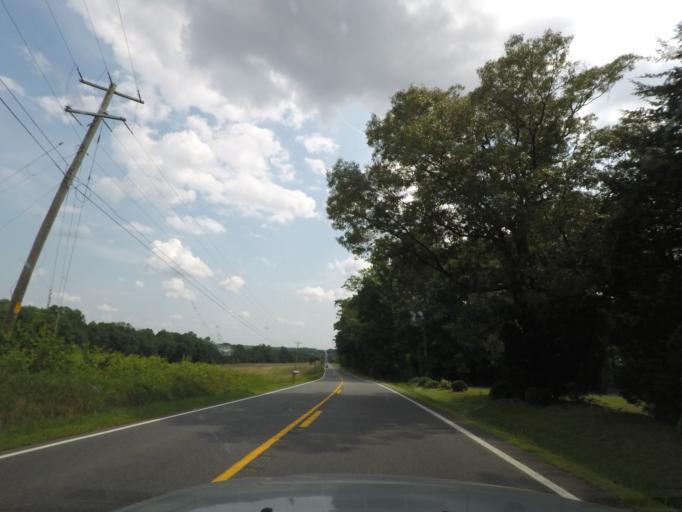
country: US
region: Virginia
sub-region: Orange County
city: Gordonsville
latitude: 38.0681
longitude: -78.1874
